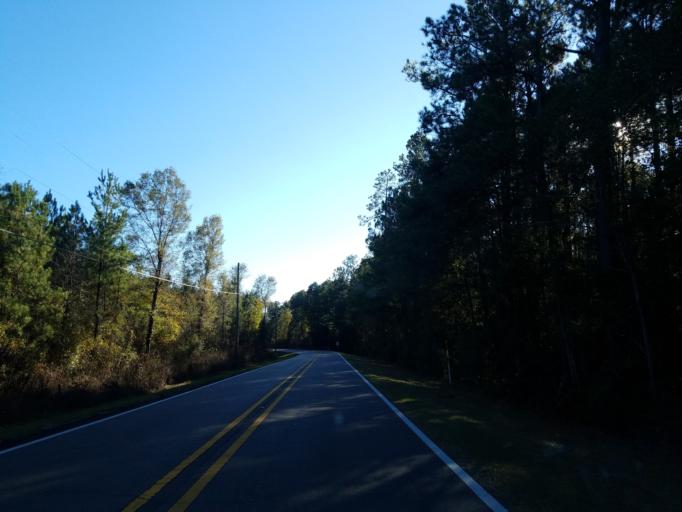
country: US
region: Mississippi
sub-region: Forrest County
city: Hattiesburg
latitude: 31.2731
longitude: -89.2923
